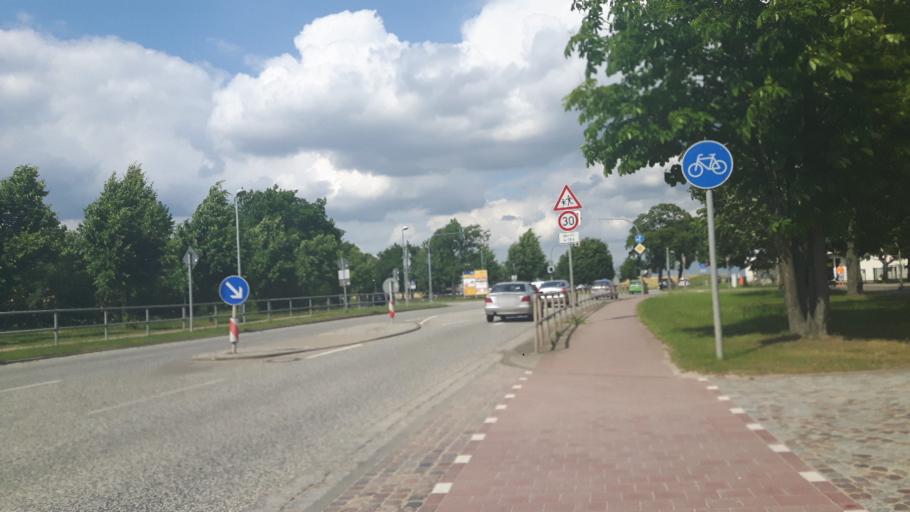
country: DE
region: Berlin
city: Buch
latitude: 52.6297
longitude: 13.5460
